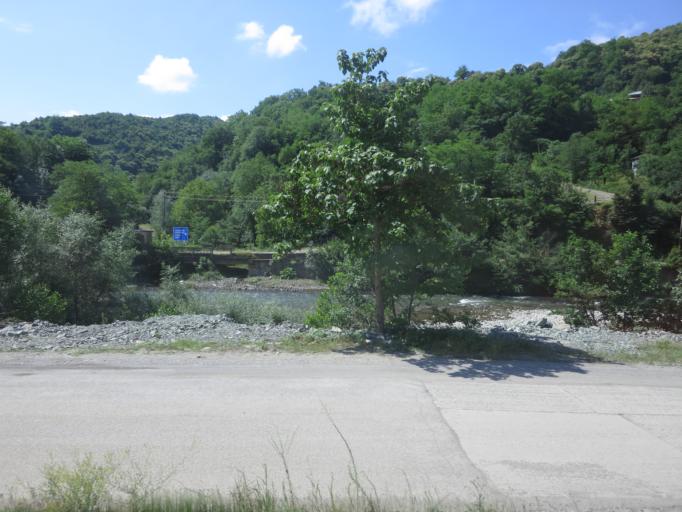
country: GE
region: Imereti
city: Kharagauli
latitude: 42.0793
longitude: 43.1584
